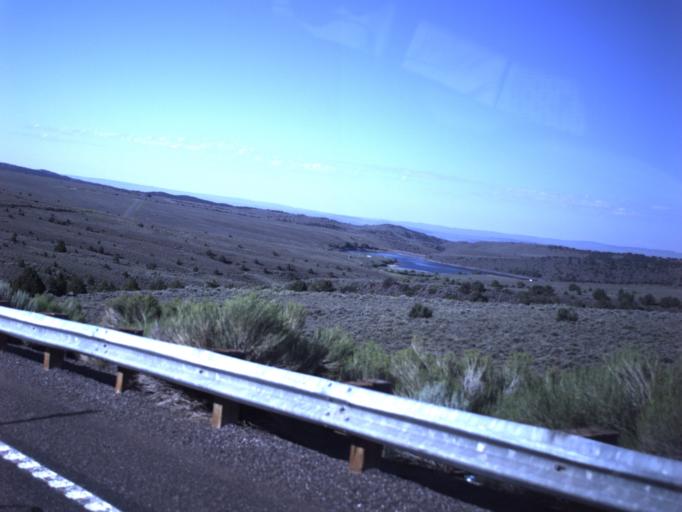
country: US
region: Utah
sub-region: Wayne County
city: Loa
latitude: 38.5353
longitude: -111.5147
